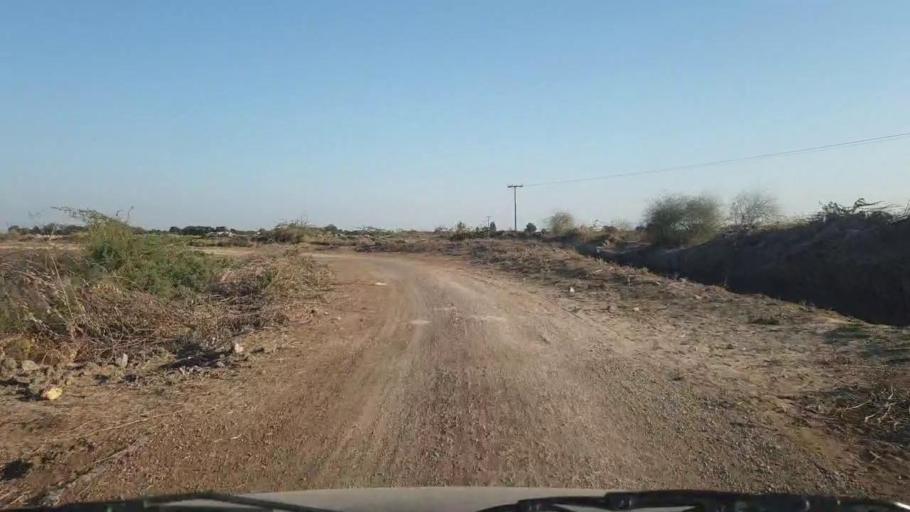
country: PK
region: Sindh
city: Samaro
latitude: 25.3262
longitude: 69.3035
